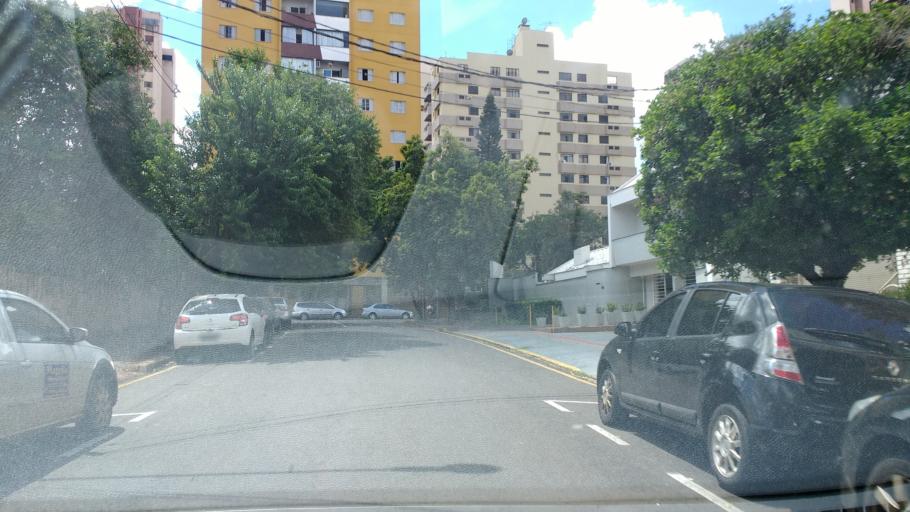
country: BR
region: Parana
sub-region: Londrina
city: Londrina
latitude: -23.3182
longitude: -51.1646
